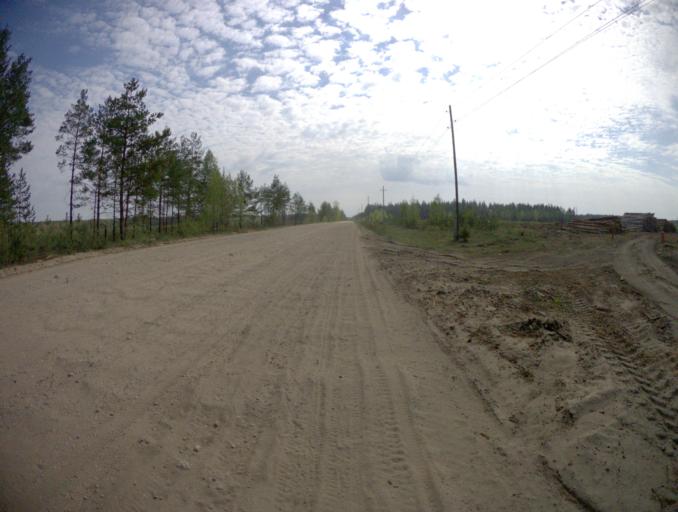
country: RU
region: Ivanovo
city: Yuzha
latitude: 56.5210
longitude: 42.0661
